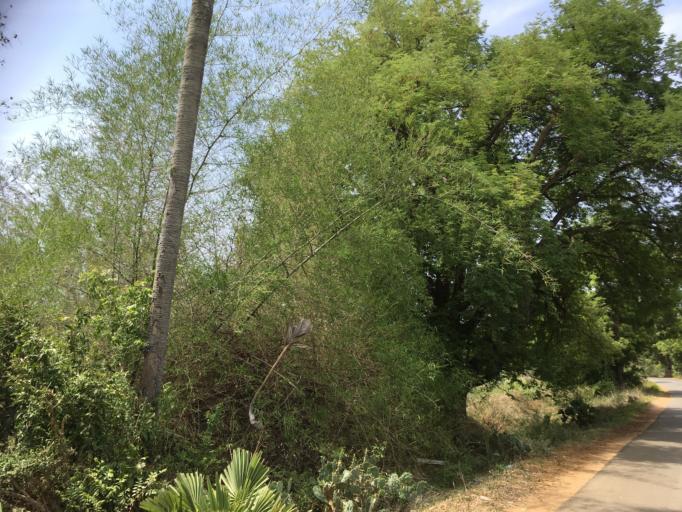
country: IN
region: Tamil Nadu
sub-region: Villupuram
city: Auroville
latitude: 12.0106
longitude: 79.7960
